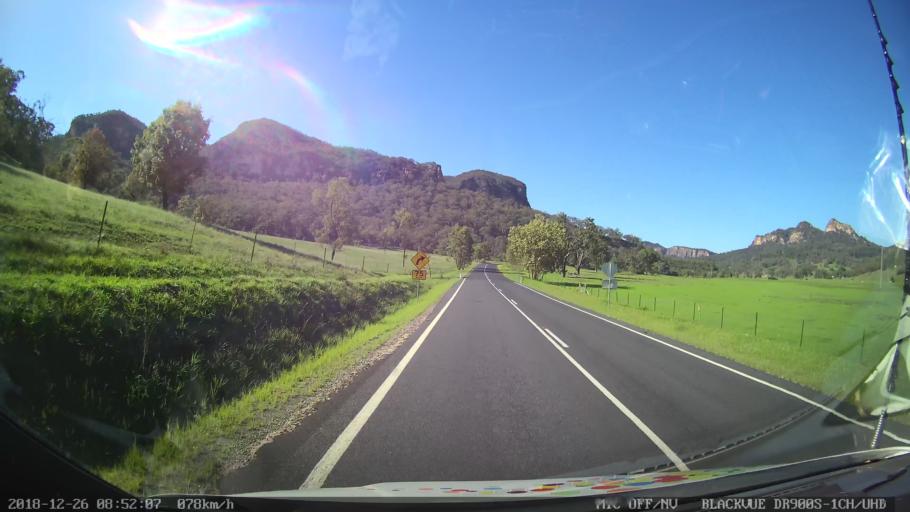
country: AU
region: New South Wales
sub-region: Mid-Western Regional
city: Kandos
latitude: -32.5933
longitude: 150.0874
